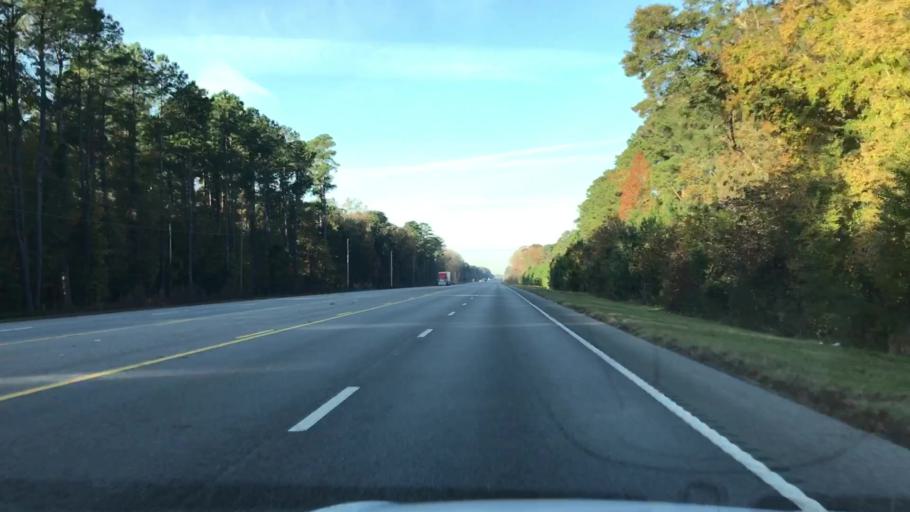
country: US
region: South Carolina
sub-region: Charleston County
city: Ravenel
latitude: 32.7708
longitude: -80.4784
